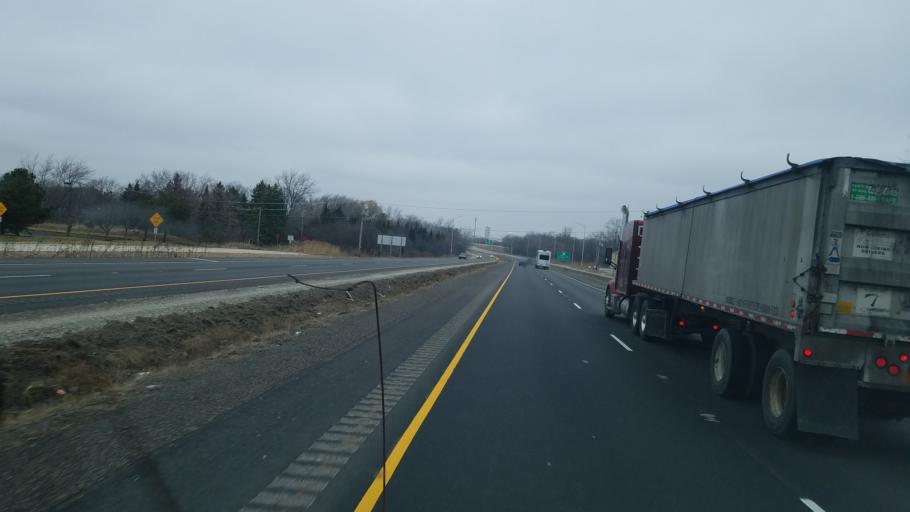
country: US
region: Illinois
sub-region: Lake County
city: Gurnee
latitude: 42.3624
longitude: -87.8947
